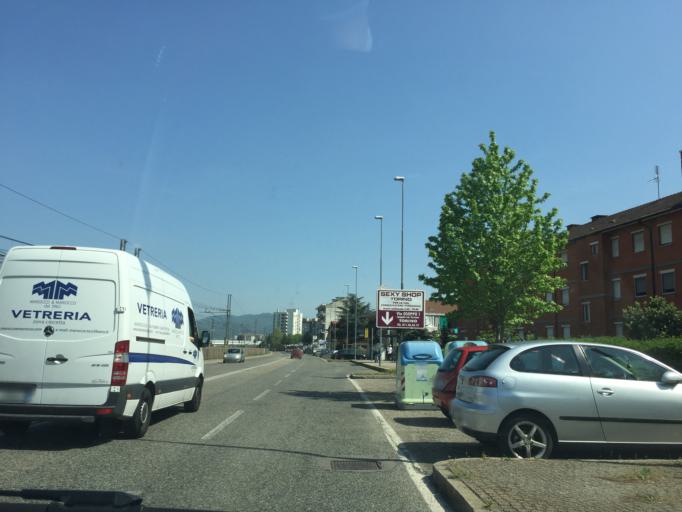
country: IT
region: Piedmont
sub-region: Provincia di Torino
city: Lesna
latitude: 45.0584
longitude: 7.6212
